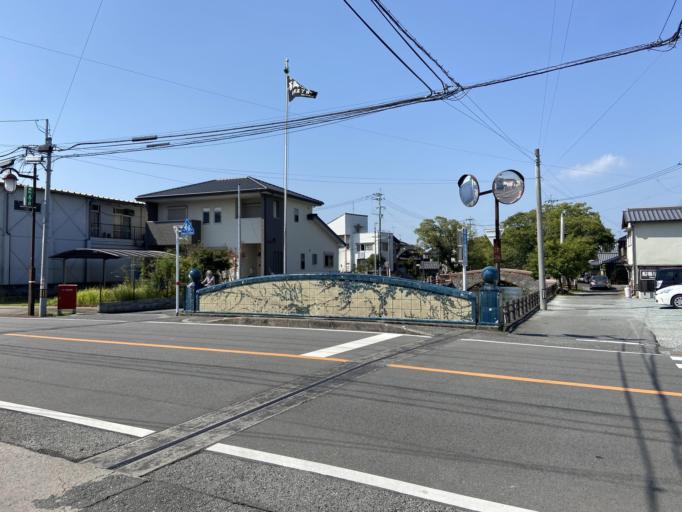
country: JP
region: Kumamoto
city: Uto
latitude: 32.6874
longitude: 130.6633
